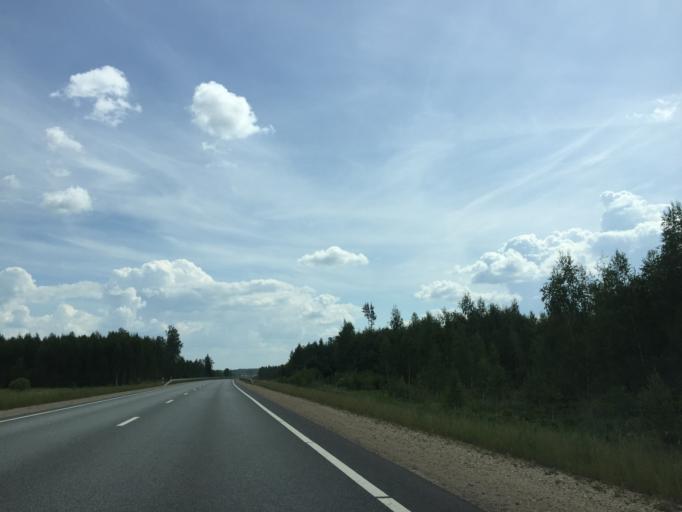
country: LV
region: Lielvarde
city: Lielvarde
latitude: 56.8152
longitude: 24.8453
